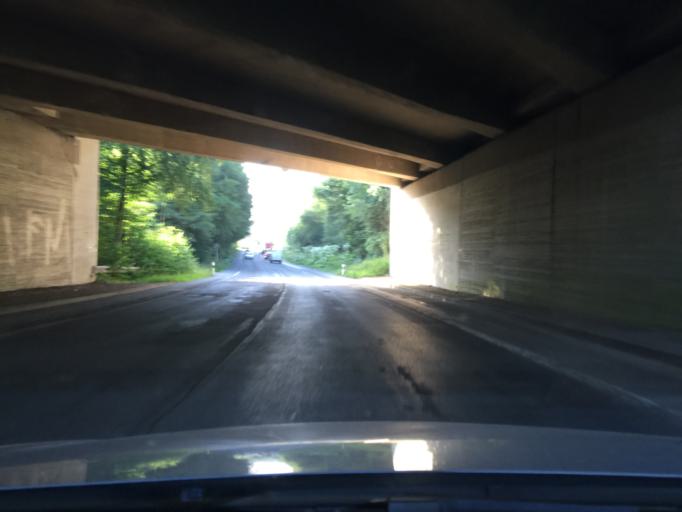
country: DE
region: North Rhine-Westphalia
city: Sprockhovel
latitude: 51.3238
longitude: 7.2695
